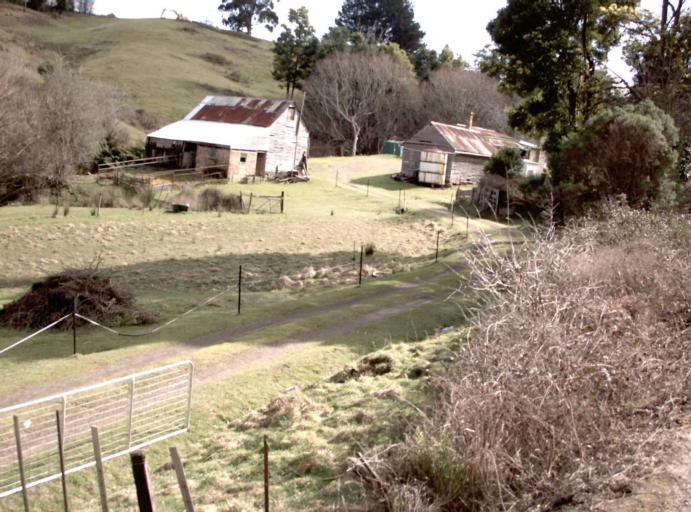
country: AU
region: Tasmania
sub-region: Launceston
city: Mayfield
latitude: -41.2465
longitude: 147.2465
